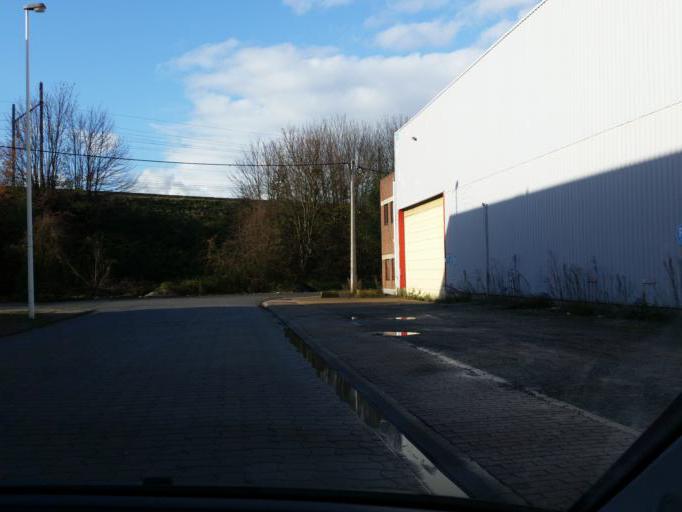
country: BE
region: Flanders
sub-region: Provincie Vlaams-Brabant
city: Diegem
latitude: 50.9079
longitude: 4.4225
